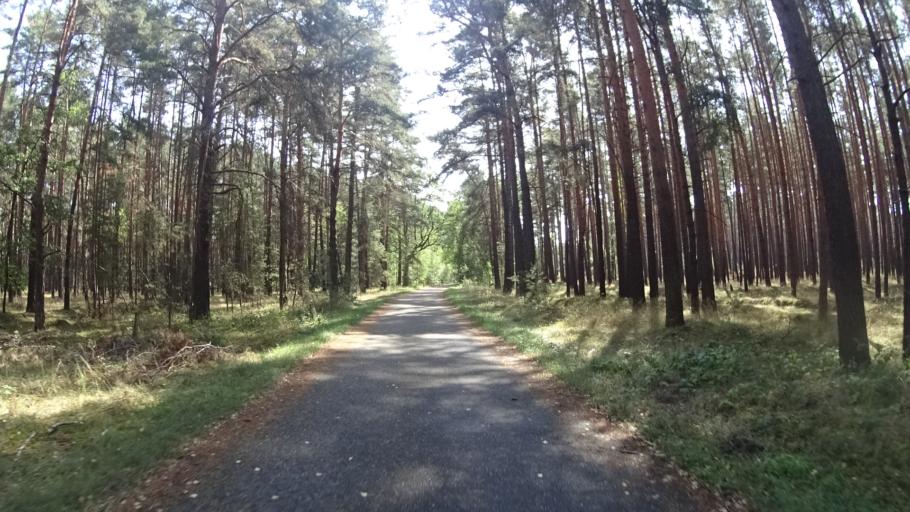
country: DE
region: Brandenburg
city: Briesen
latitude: 51.8053
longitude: 14.2805
